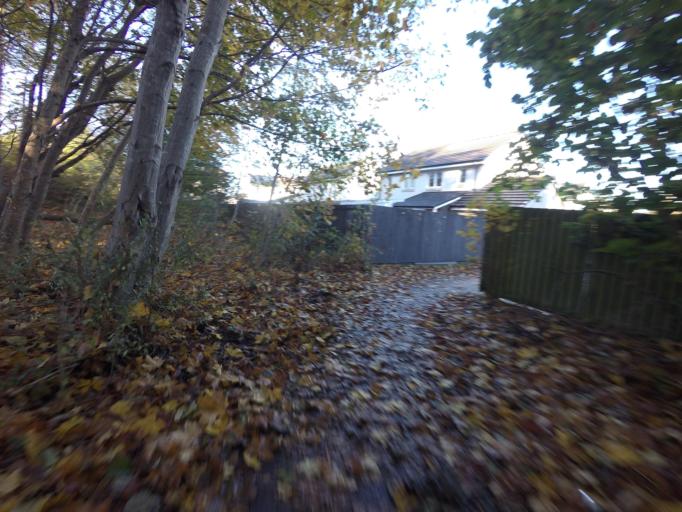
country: GB
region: Scotland
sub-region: West Lothian
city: Mid Calder
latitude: 55.9041
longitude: -3.4948
